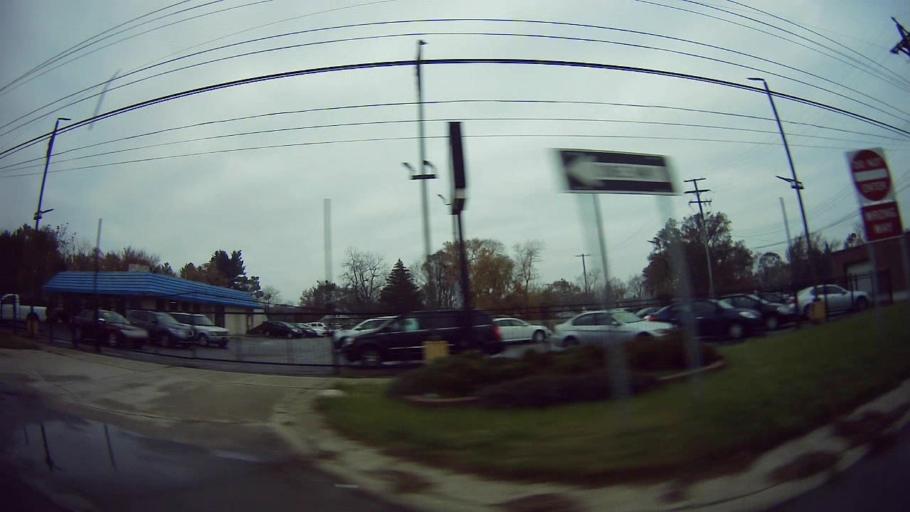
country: US
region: Michigan
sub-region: Wayne County
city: Redford
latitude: 42.4040
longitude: -83.2771
